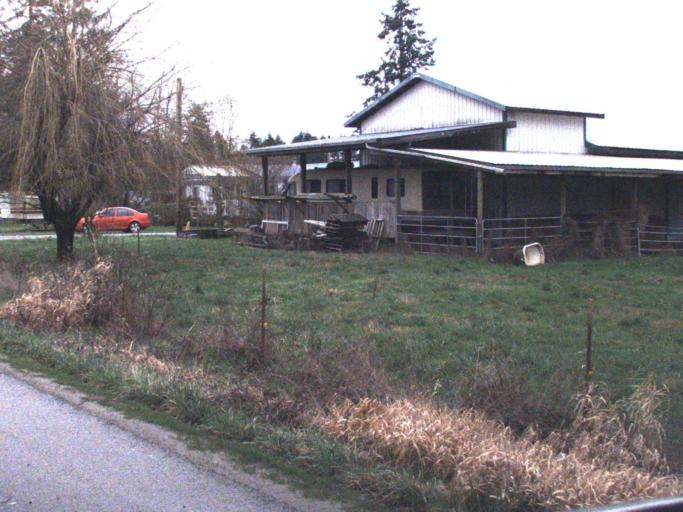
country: US
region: Washington
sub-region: Snohomish County
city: Smokey Point
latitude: 48.1520
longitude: -122.2028
